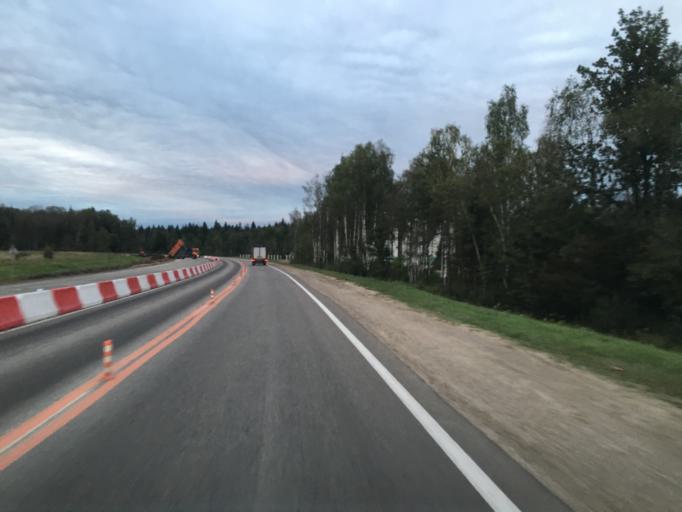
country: RU
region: Kaluga
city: Detchino
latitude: 54.6810
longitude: 36.2992
